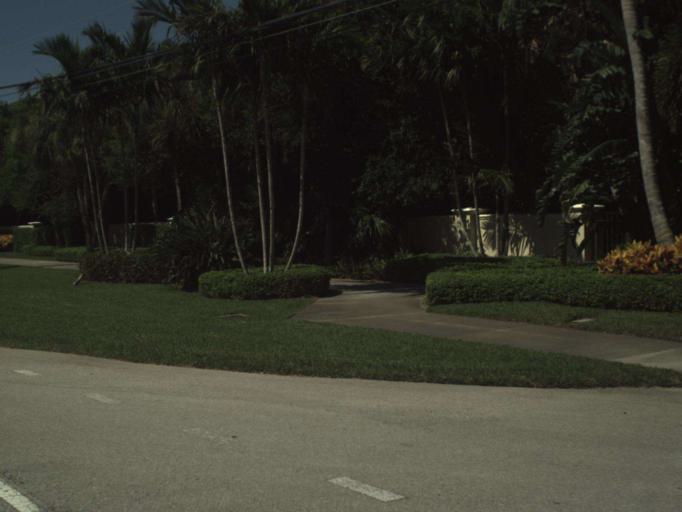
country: US
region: Florida
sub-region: Indian River County
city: Indian River Shores
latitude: 27.7356
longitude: -80.3840
